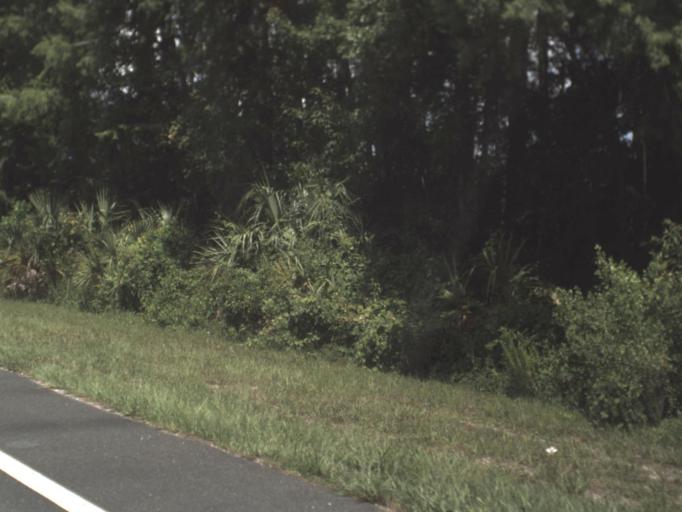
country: US
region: Florida
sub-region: Levy County
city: Chiefland
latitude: 29.2156
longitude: -82.9697
